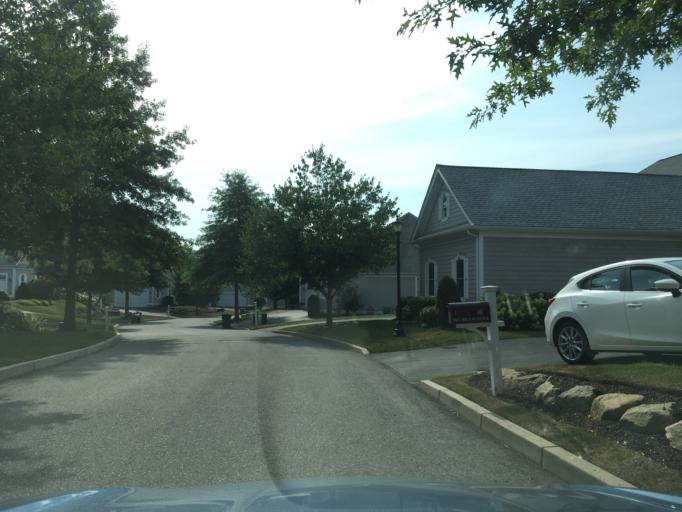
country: US
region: Rhode Island
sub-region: Kent County
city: East Greenwich
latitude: 41.6480
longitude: -71.4982
